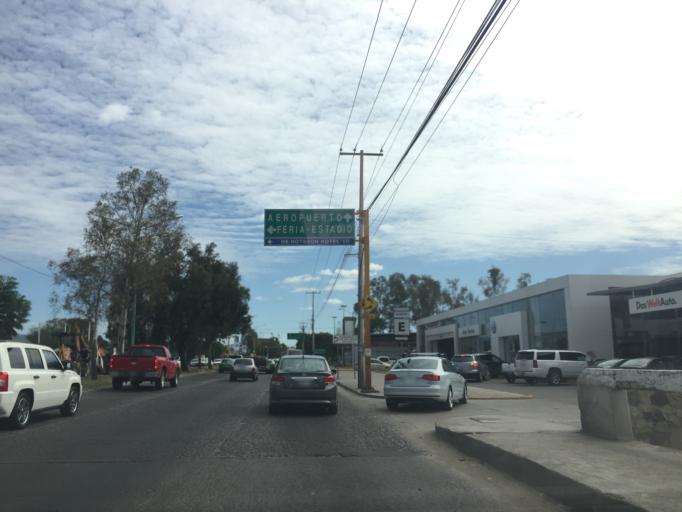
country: MX
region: Guanajuato
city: Leon
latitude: 21.0977
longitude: -101.6649
